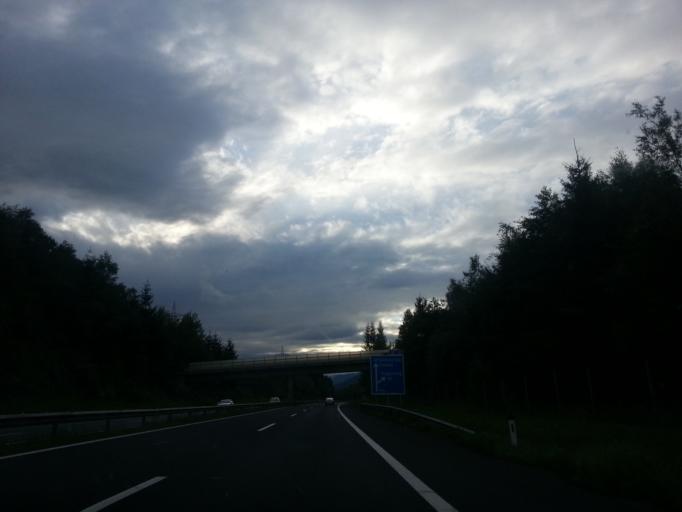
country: AT
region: Styria
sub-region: Politischer Bezirk Liezen
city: Treglwang
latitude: 47.4707
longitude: 14.6211
